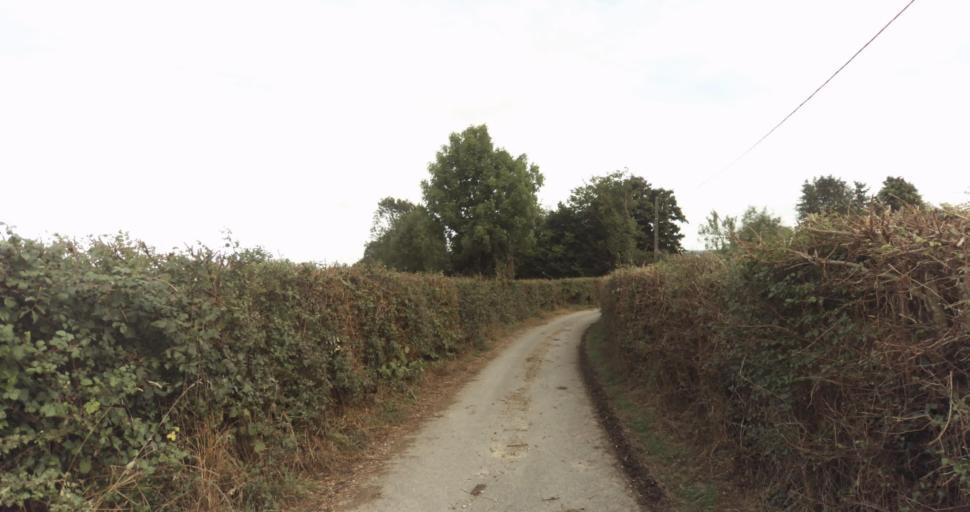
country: FR
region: Lower Normandy
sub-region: Departement de l'Orne
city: Gace
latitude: 48.8650
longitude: 0.2649
